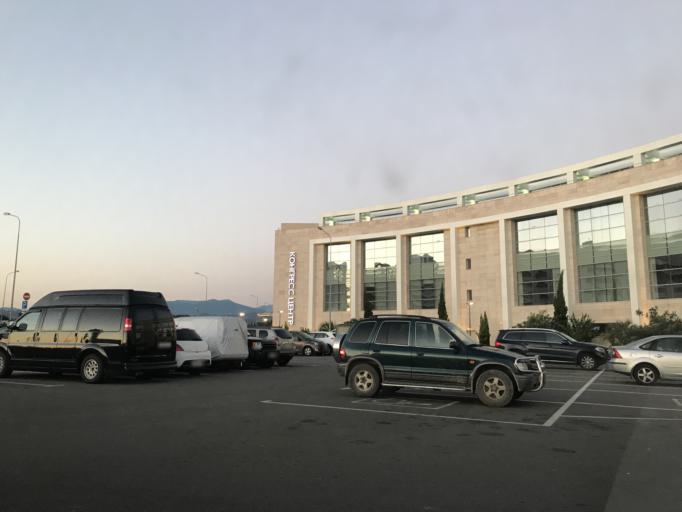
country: RU
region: Krasnodarskiy
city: Adler
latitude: 43.4104
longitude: 39.9363
